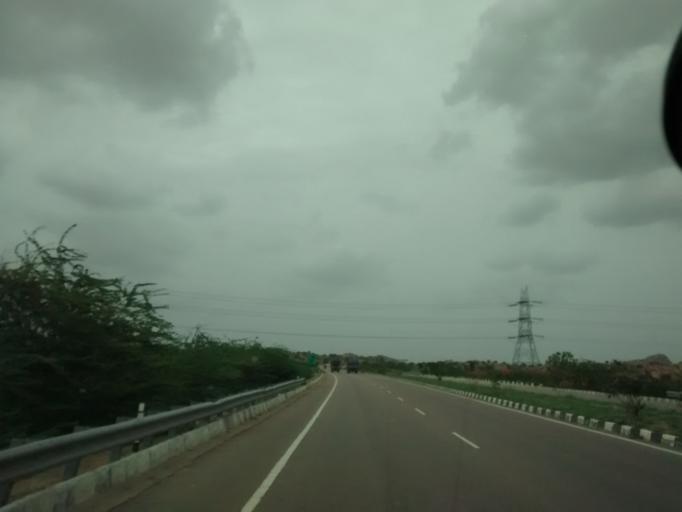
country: IN
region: Andhra Pradesh
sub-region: Kurnool
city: Ramapuram
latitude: 15.1493
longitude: 77.6659
